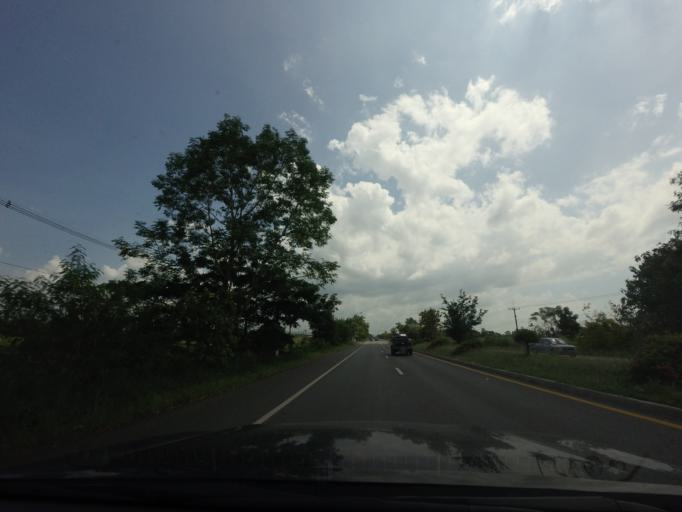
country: TH
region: Phetchabun
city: Phetchabun
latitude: 16.2378
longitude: 101.0792
